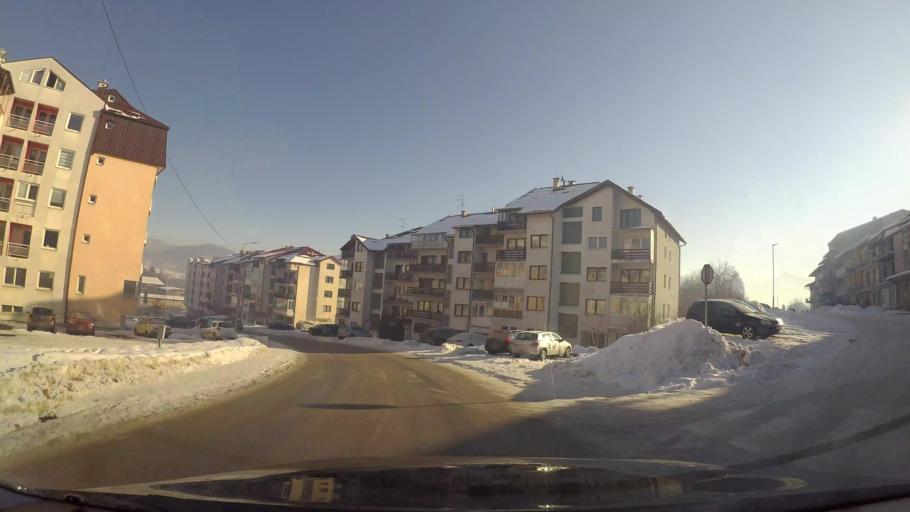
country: BA
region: Federation of Bosnia and Herzegovina
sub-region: Kanton Sarajevo
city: Sarajevo
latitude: 43.8223
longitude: 18.3707
